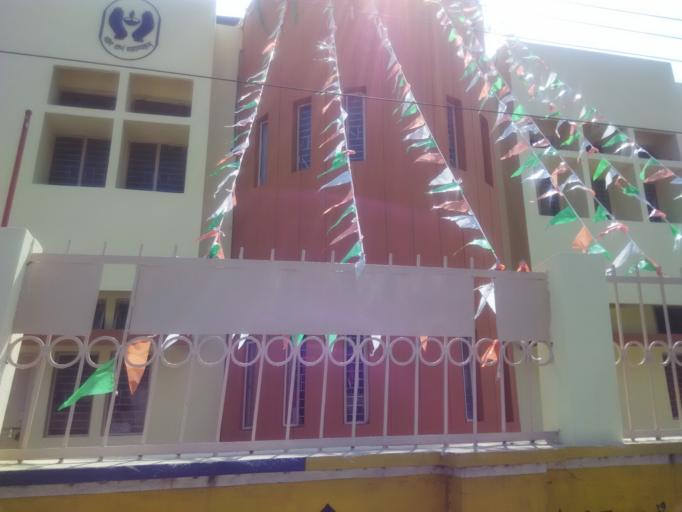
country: IN
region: Andhra Pradesh
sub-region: Prakasam
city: Chirala
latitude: 15.8311
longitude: 80.3535
